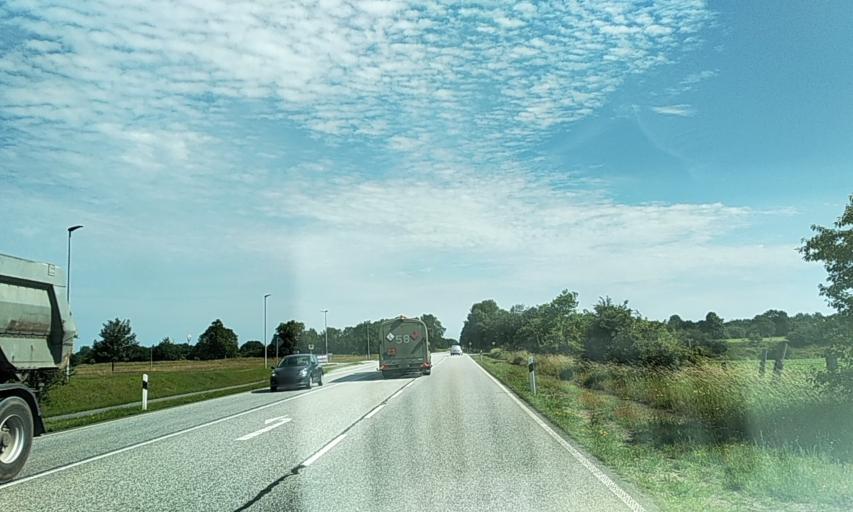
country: DE
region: Schleswig-Holstein
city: Jagel
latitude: 54.4700
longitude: 9.5429
